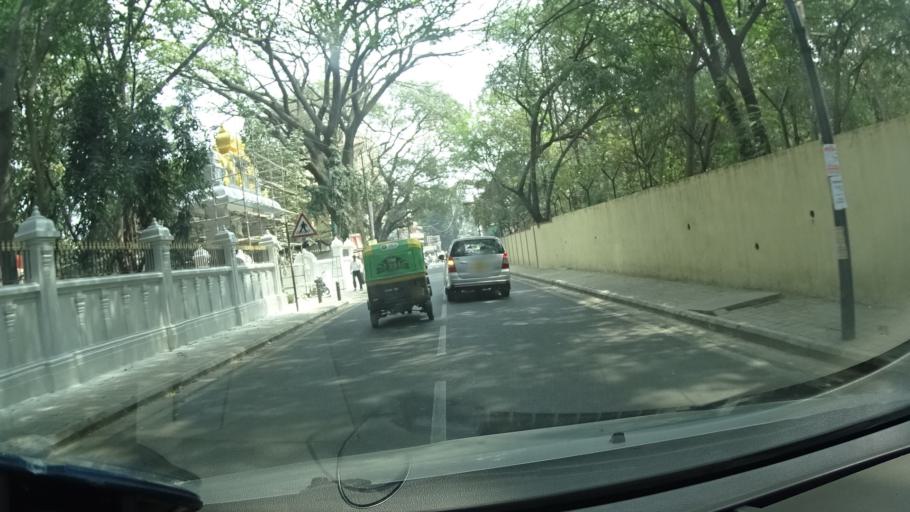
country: IN
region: Karnataka
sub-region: Bangalore Urban
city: Bangalore
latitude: 12.9902
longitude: 77.5922
